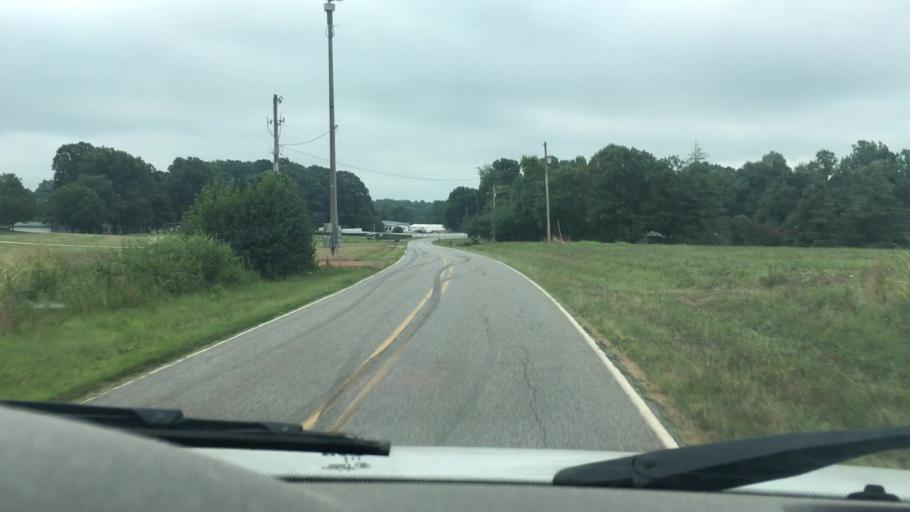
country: US
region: North Carolina
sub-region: Gaston County
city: Davidson
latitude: 35.5317
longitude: -80.8295
